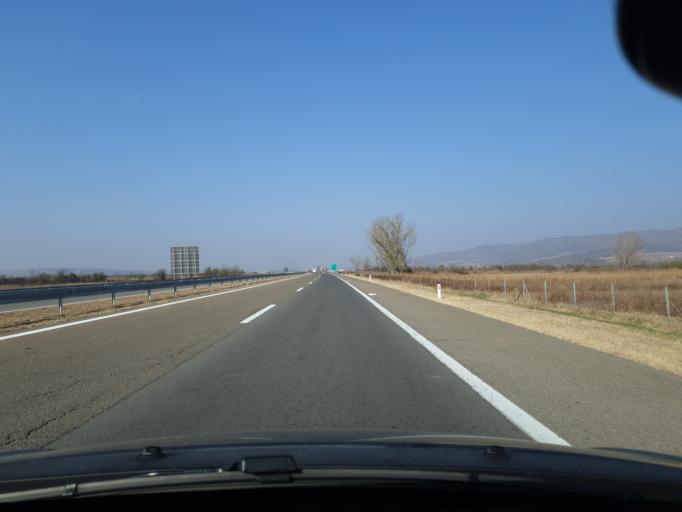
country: RS
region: Central Serbia
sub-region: Nisavski Okrug
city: Doljevac
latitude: 43.1568
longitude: 21.8904
